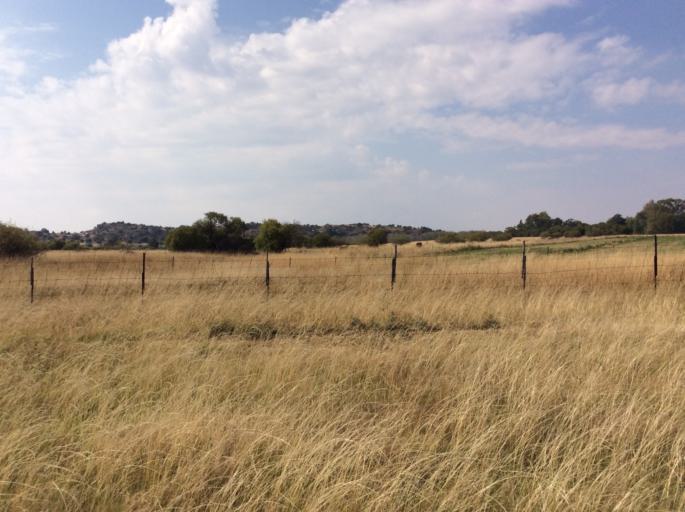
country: LS
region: Mafeteng
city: Mafeteng
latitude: -29.9841
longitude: 27.0104
